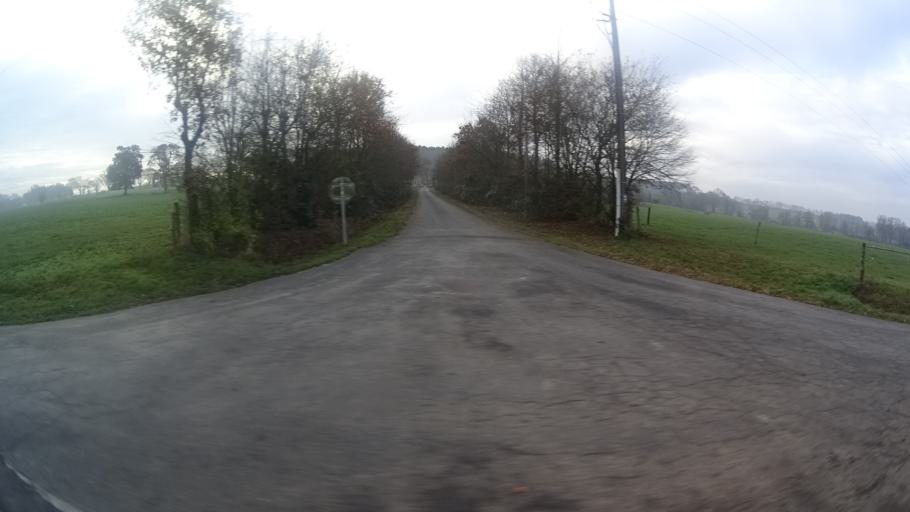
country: FR
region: Pays de la Loire
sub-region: Departement de la Loire-Atlantique
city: Avessac
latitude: 47.6523
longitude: -2.0050
